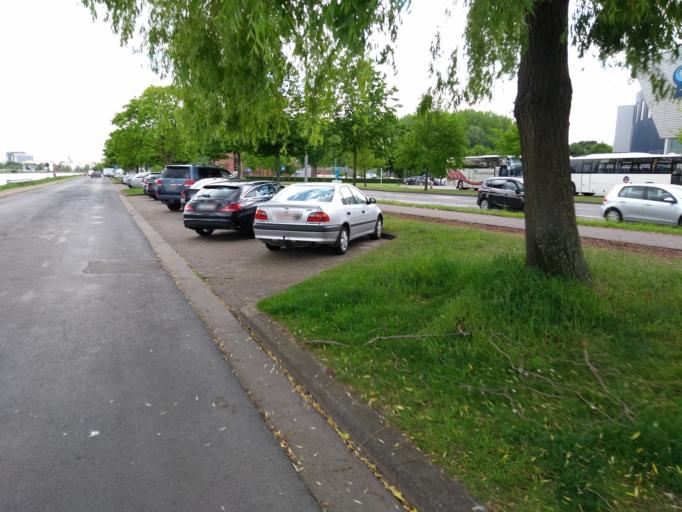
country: BE
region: Flanders
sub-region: Provincie Oost-Vlaanderen
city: Gent
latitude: 51.0499
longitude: 3.6858
